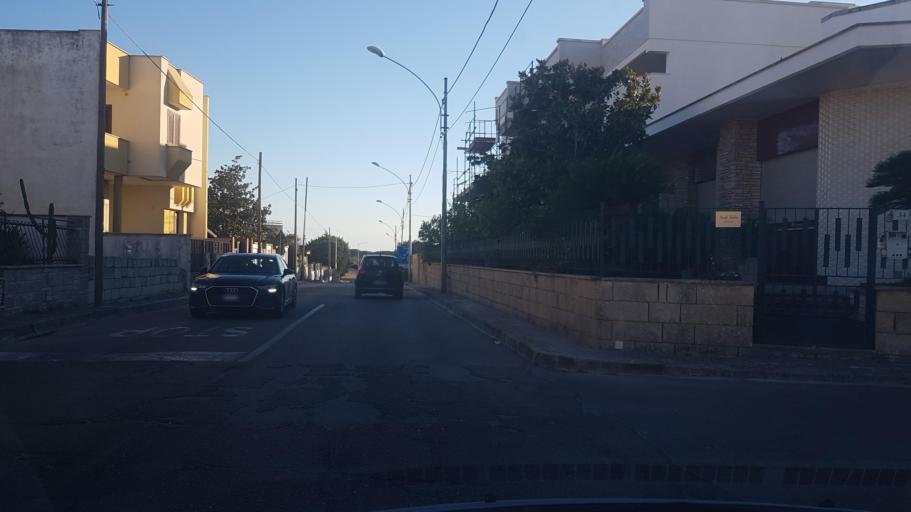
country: IT
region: Apulia
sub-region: Provincia di Lecce
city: Struda
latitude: 40.3167
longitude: 18.2797
